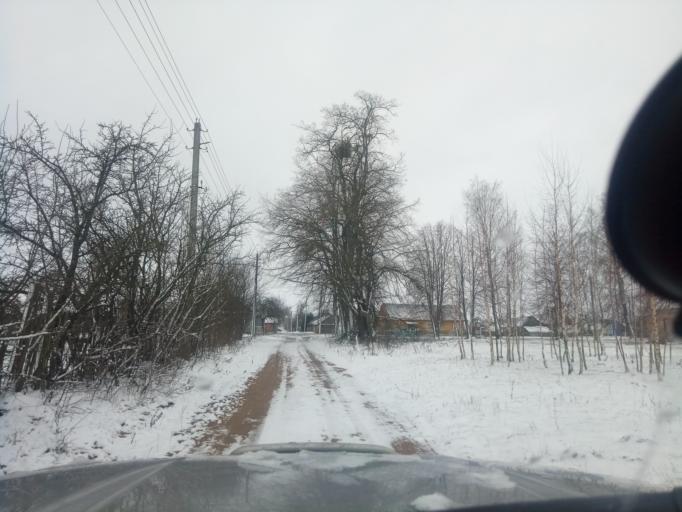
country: BY
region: Minsk
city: Klyetsk
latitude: 53.0237
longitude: 26.7145
